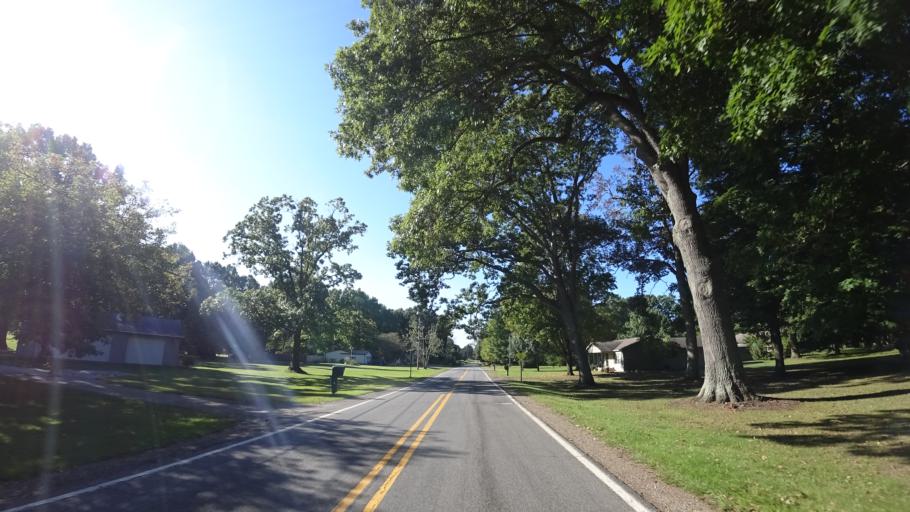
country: US
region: Michigan
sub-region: Berrien County
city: Lake Michigan Beach
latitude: 42.1779
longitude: -86.3846
